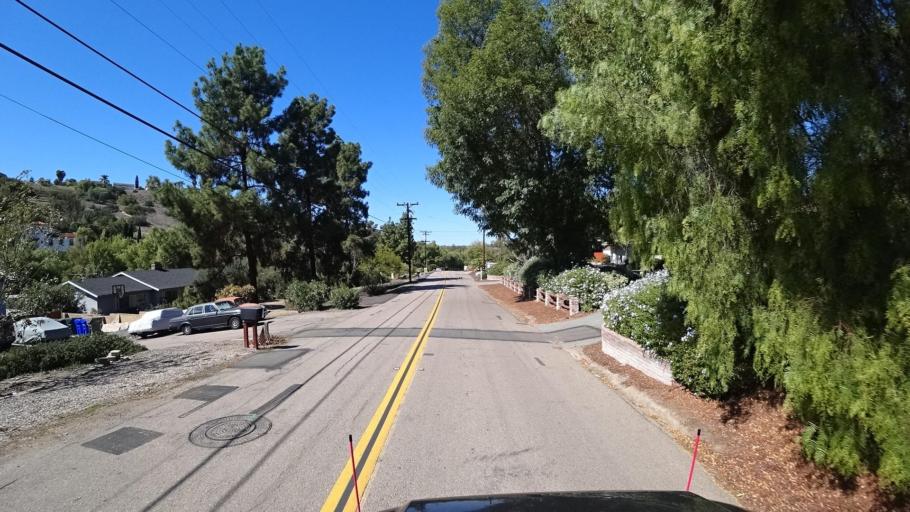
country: US
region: California
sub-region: San Diego County
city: Bonita
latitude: 32.6594
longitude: -117.0193
